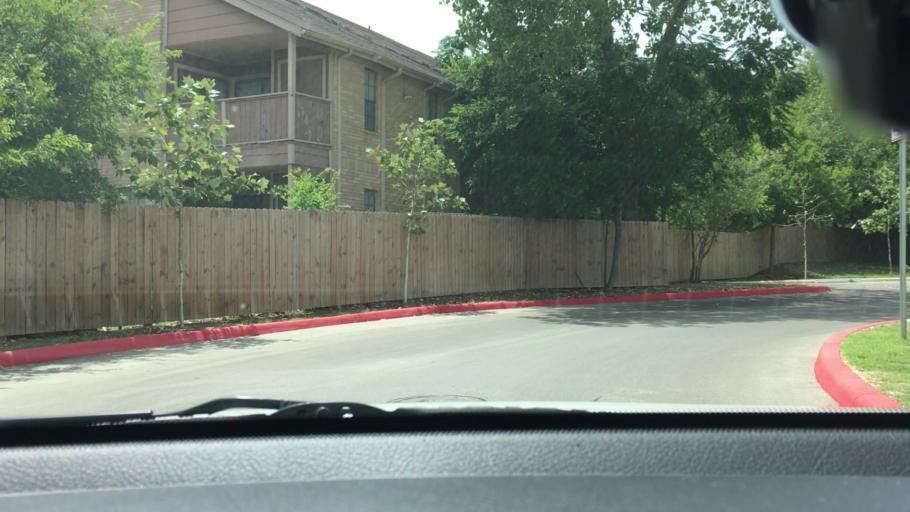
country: US
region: Texas
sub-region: Bexar County
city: Live Oak
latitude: 29.5731
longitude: -98.3766
